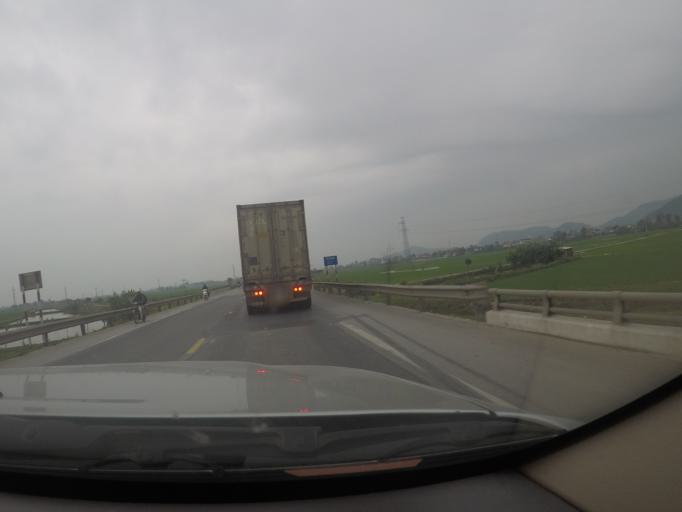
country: VN
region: Nghe An
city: Quan Hanh
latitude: 18.7356
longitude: 105.6324
